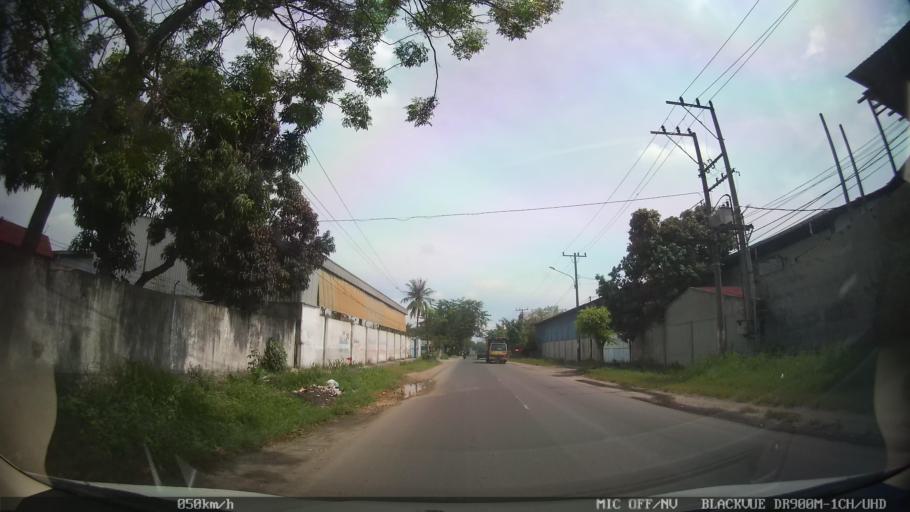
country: ID
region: North Sumatra
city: Medan
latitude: 3.6413
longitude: 98.7166
